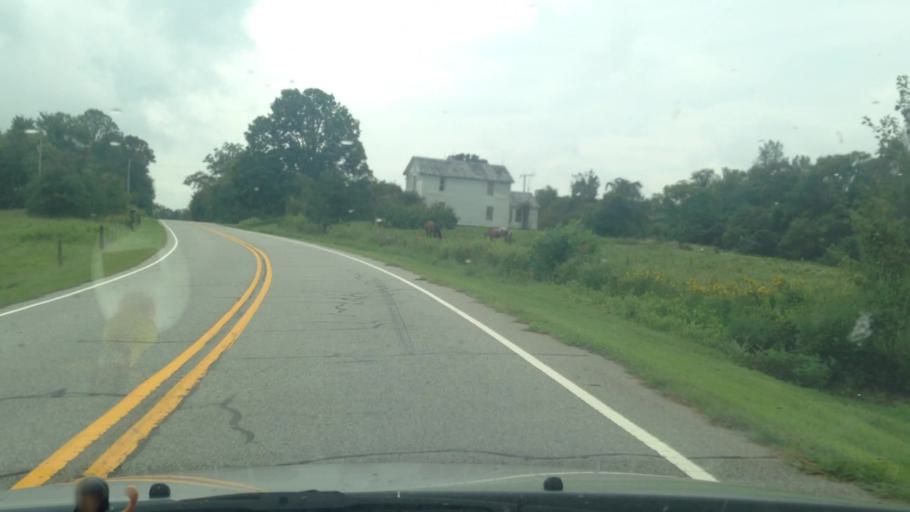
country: US
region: North Carolina
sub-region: Stokes County
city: Danbury
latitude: 36.4219
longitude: -80.1108
